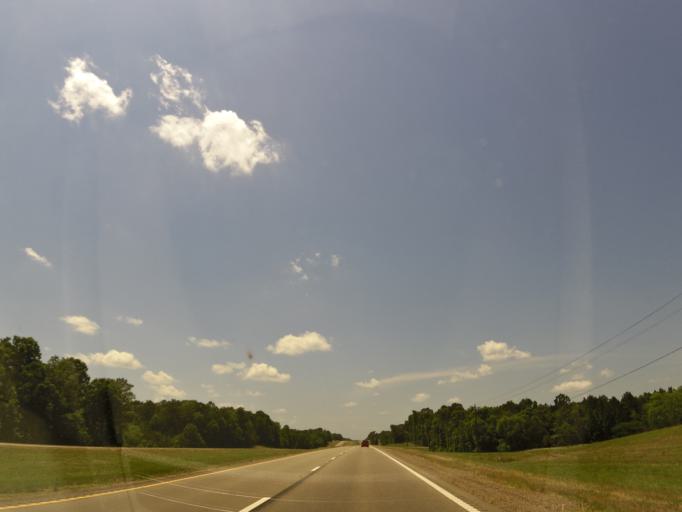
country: US
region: Mississippi
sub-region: Pontotoc County
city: Pontotoc
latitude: 34.2975
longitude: -89.2309
